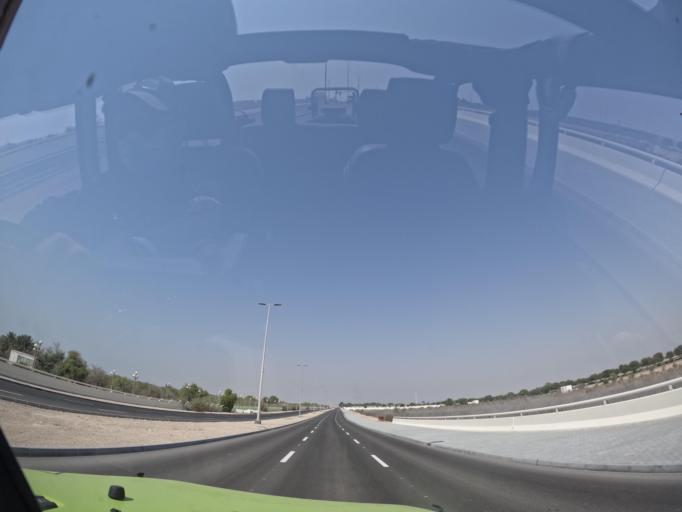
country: AE
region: Abu Dhabi
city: Abu Dhabi
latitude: 24.4667
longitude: 54.6264
